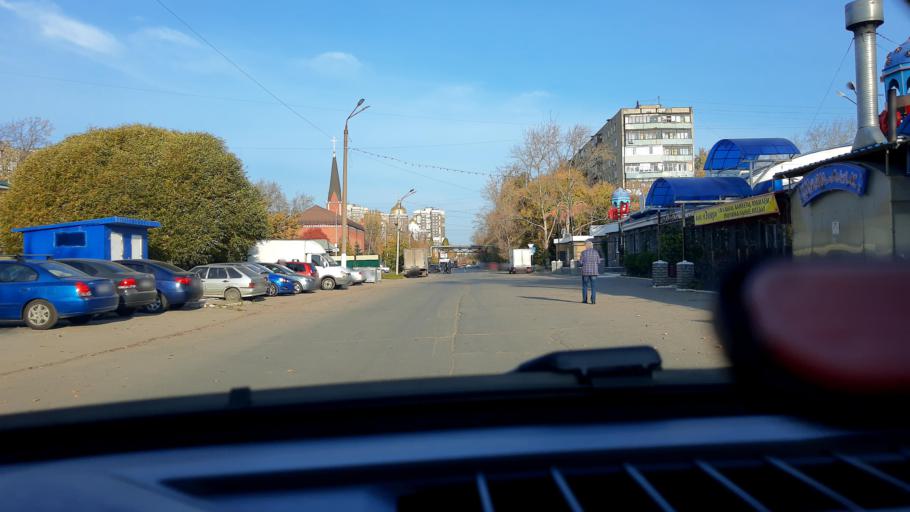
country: RU
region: Nizjnij Novgorod
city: Nizhniy Novgorod
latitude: 56.2584
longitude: 43.8853
